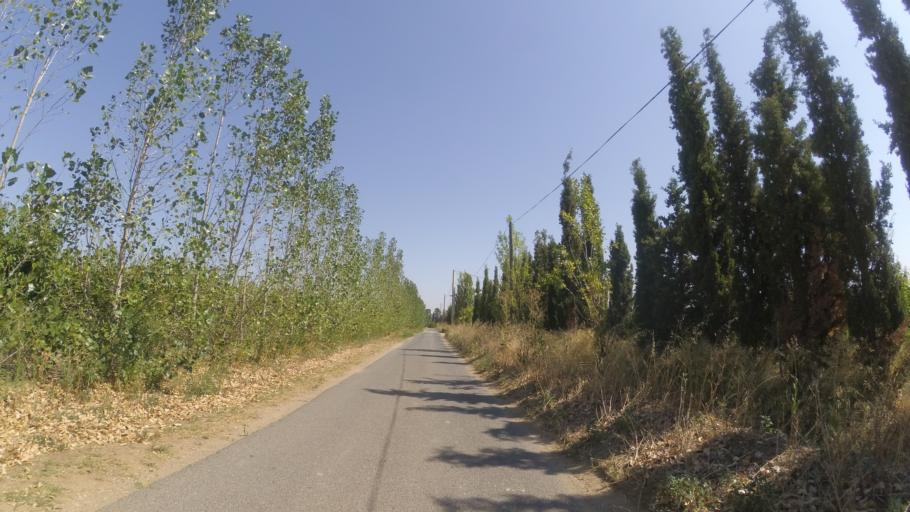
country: FR
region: Languedoc-Roussillon
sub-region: Departement des Pyrenees-Orientales
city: Corneilla-la-Riviere
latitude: 42.6593
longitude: 2.7200
